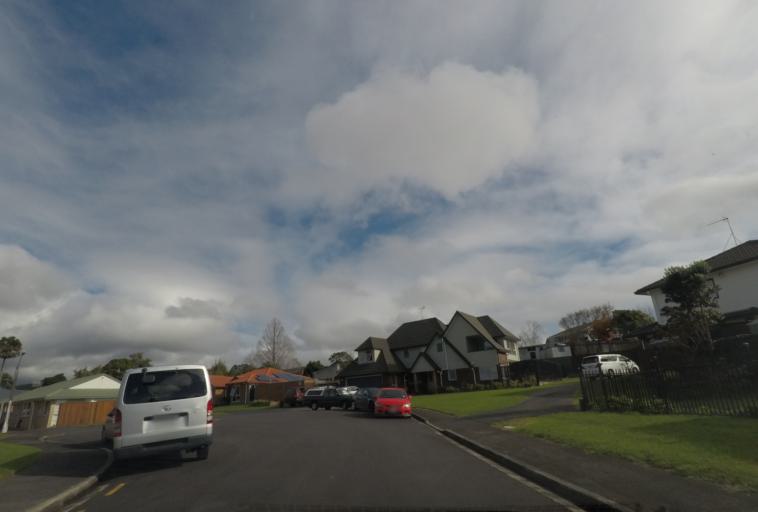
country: NZ
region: Auckland
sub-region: Auckland
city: Waitakere
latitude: -36.8988
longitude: 174.6530
